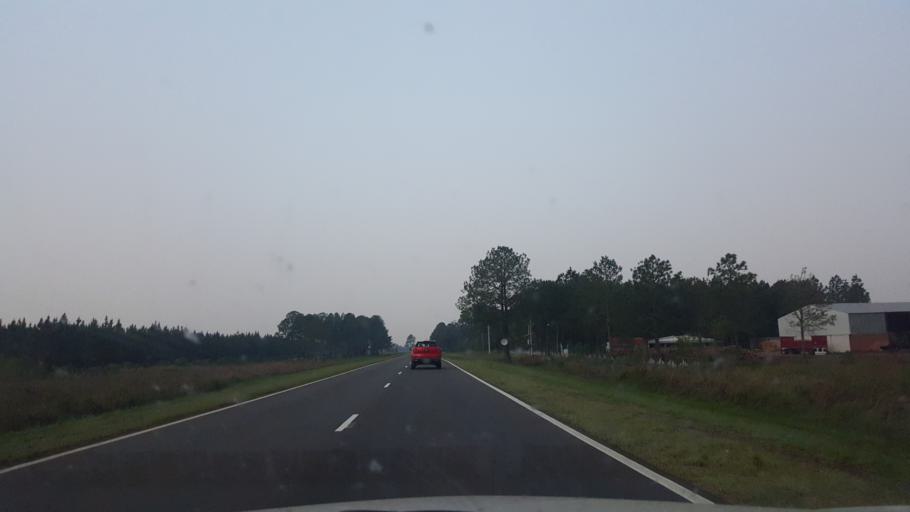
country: PY
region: Misiones
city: Ayolas
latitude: -27.6246
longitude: -56.9312
